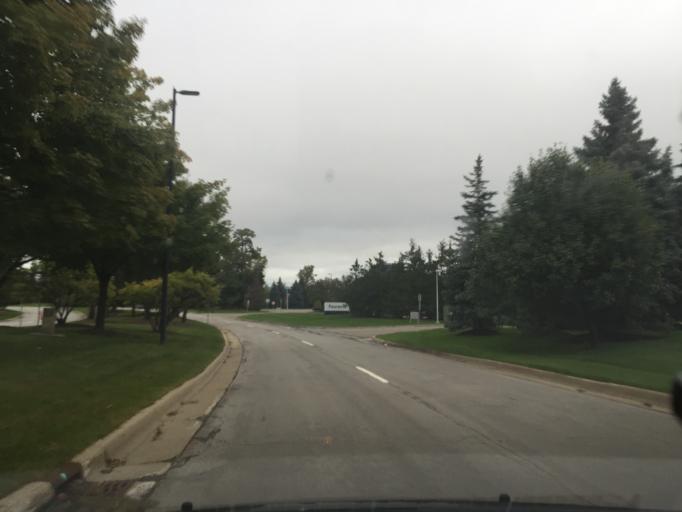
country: US
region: Michigan
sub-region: Oakland County
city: Auburn Hills
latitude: 42.6457
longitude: -83.2423
